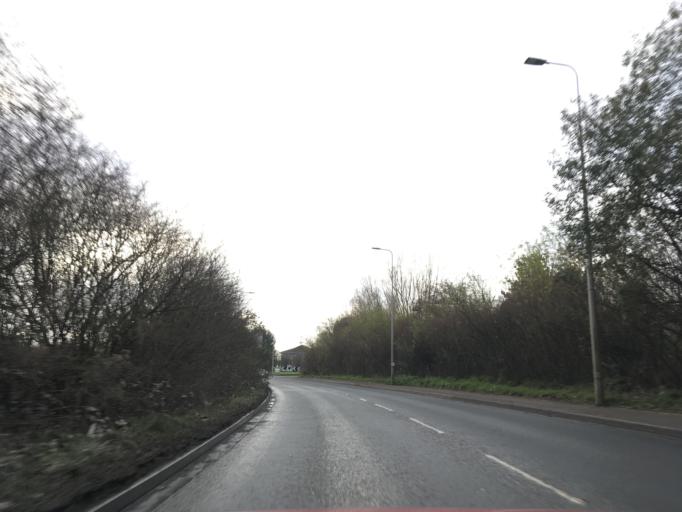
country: GB
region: Wales
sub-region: Cardiff
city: Cardiff
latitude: 51.4947
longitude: -3.1318
